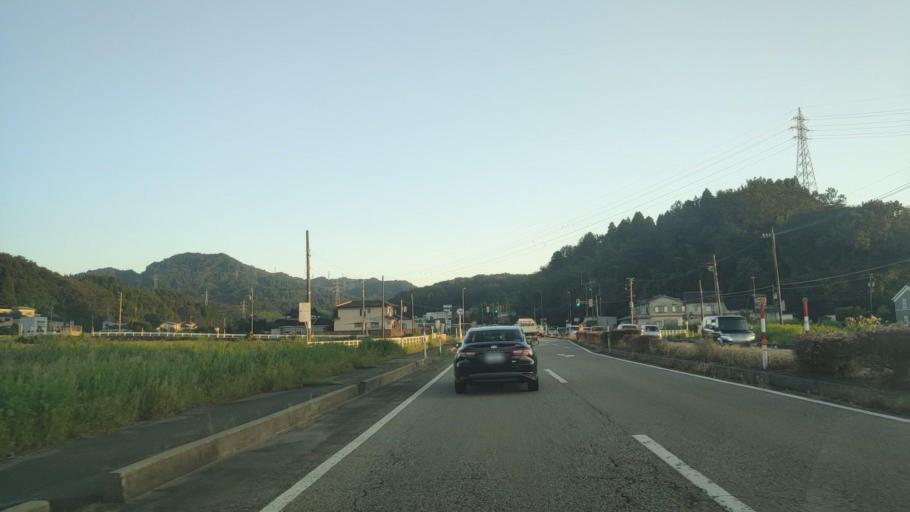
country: JP
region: Toyama
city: Himi
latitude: 36.8111
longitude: 136.9967
